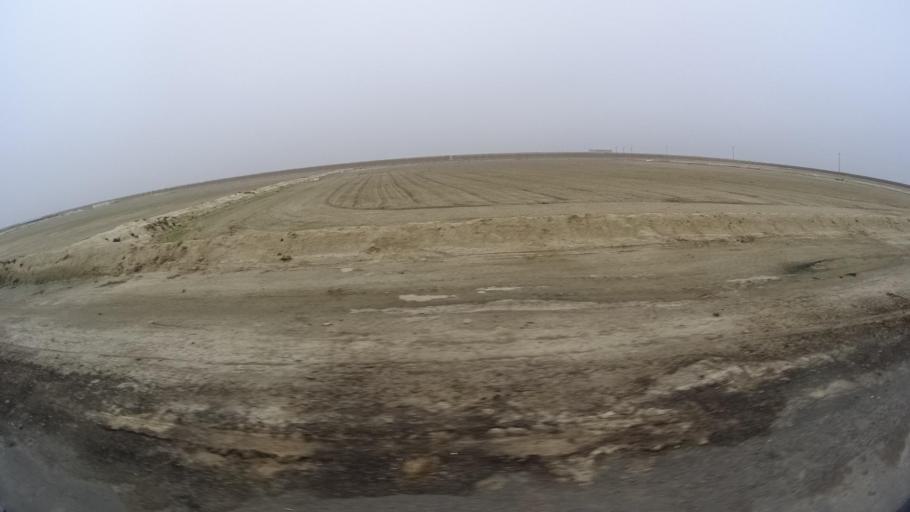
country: US
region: California
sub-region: Tulare County
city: Alpaugh
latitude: 35.7629
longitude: -119.4012
